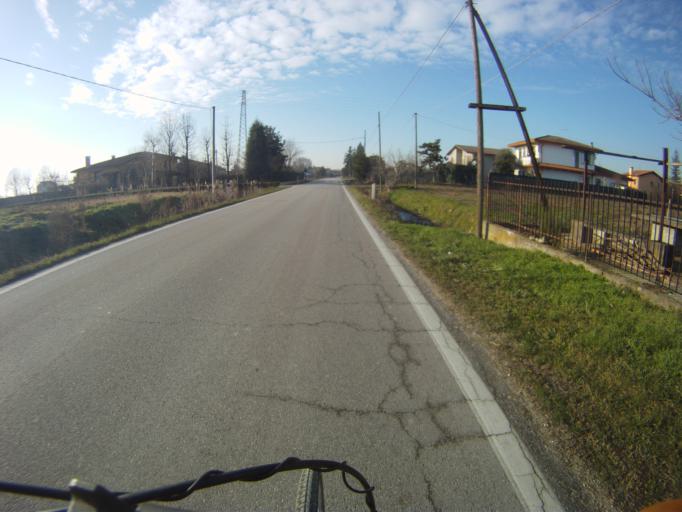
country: IT
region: Veneto
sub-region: Provincia di Padova
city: Piove di Sacco-Piovega
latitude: 45.2889
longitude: 12.0180
